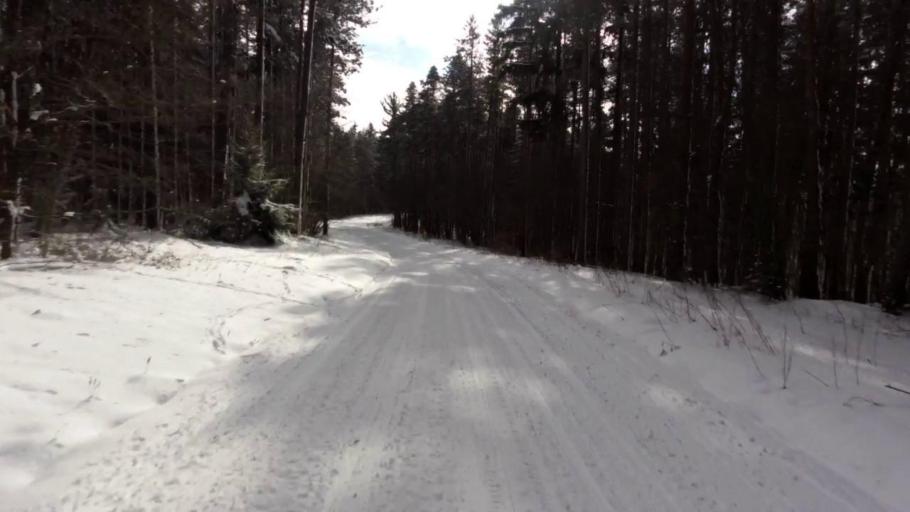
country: US
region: Pennsylvania
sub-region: McKean County
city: Bradford
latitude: 42.0285
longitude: -78.7136
